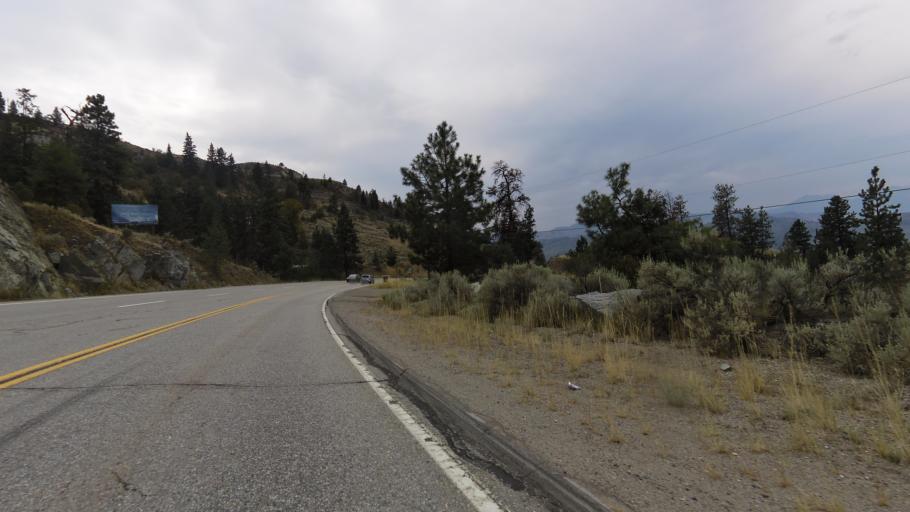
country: CA
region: British Columbia
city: Osoyoos
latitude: 49.0156
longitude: -119.4033
